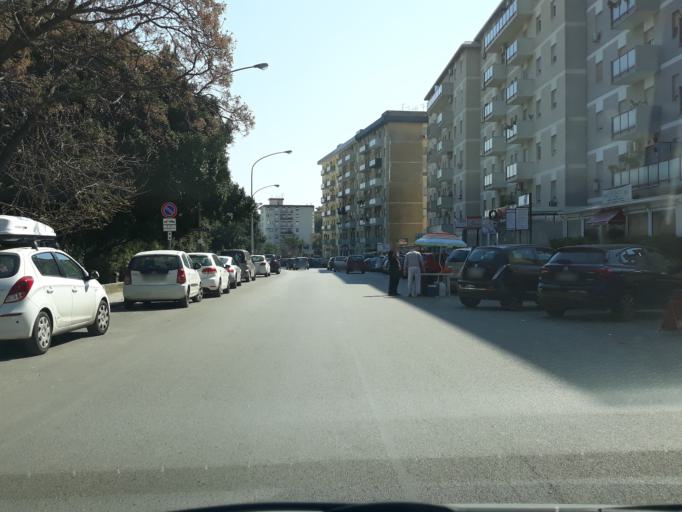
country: IT
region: Sicily
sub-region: Palermo
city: Piano dei Geli
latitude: 38.1256
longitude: 13.2924
